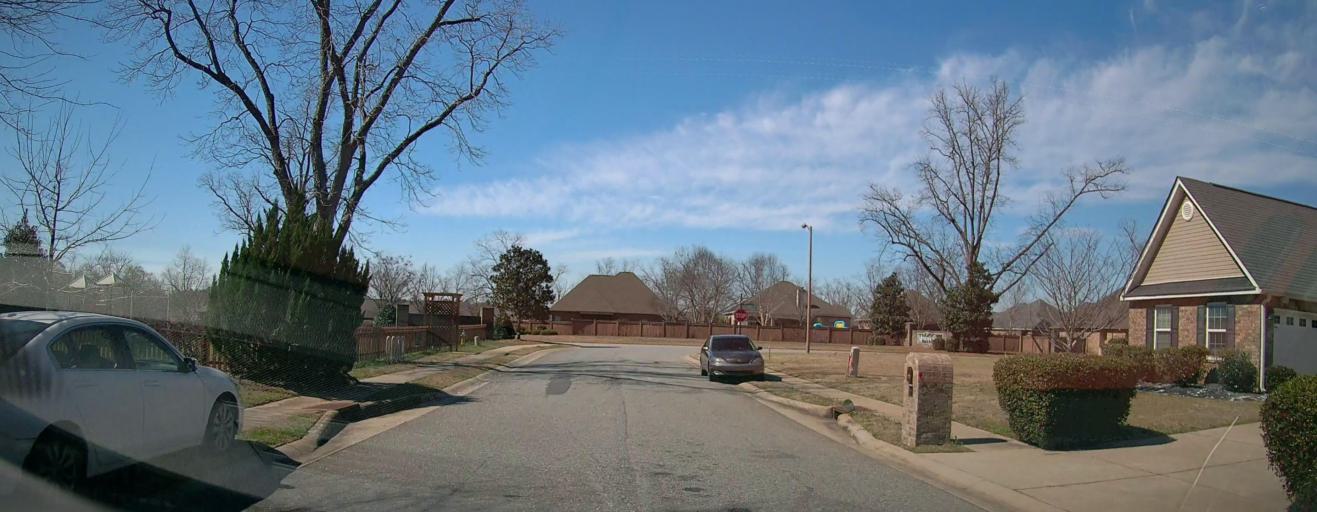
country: US
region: Georgia
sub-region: Houston County
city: Perry
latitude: 32.4953
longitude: -83.6586
